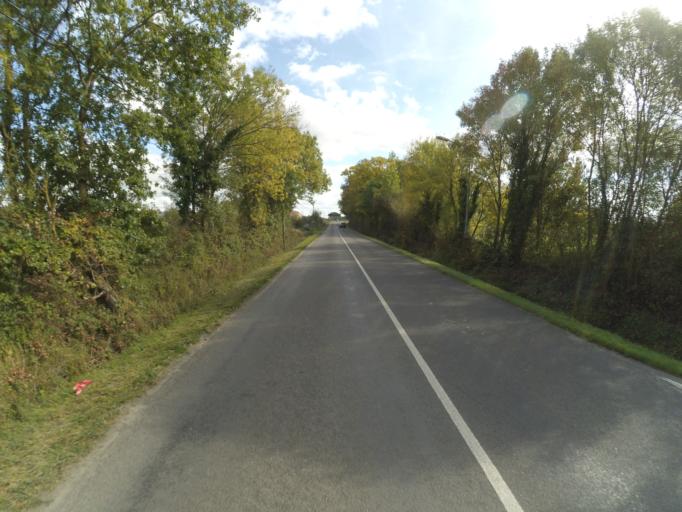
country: FR
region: Pays de la Loire
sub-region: Departement de la Loire-Atlantique
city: Gorges
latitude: 47.1040
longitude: -1.3218
